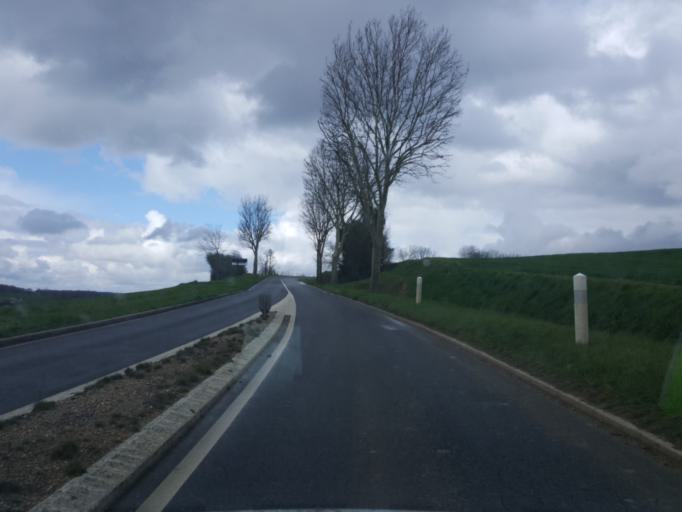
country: FR
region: Ile-de-France
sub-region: Departement du Val-d'Oise
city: Magny-en-Vexin
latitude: 49.1358
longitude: 1.7899
